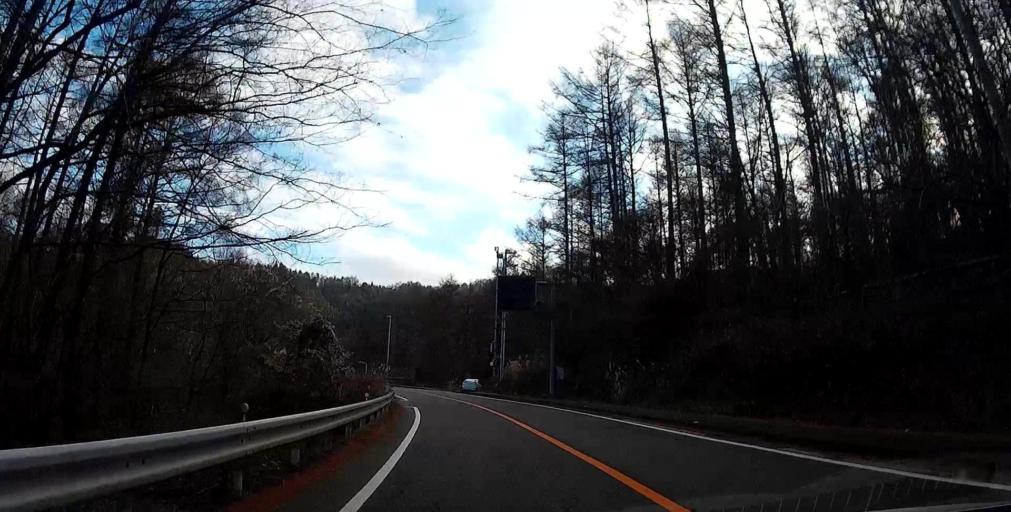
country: JP
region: Yamanashi
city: Fujikawaguchiko
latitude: 35.4760
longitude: 138.8351
